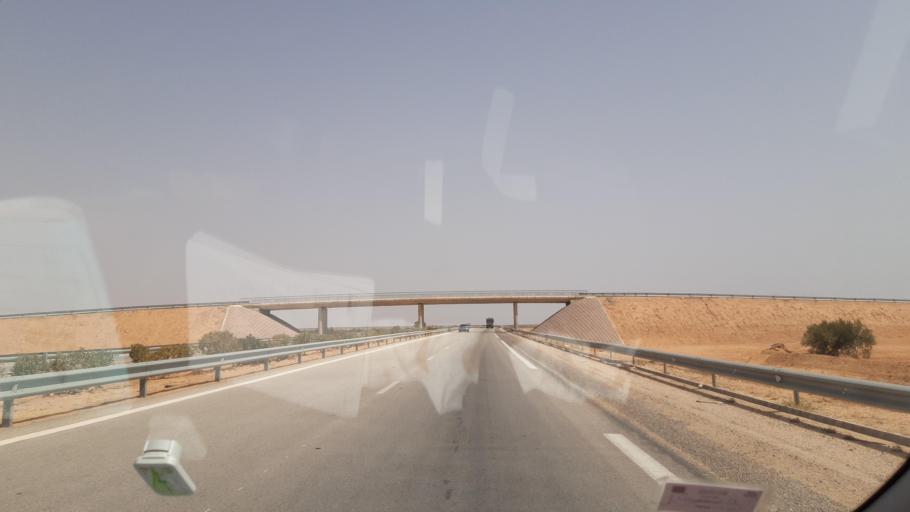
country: TN
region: Safaqis
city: Bi'r `Ali Bin Khalifah
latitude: 34.5285
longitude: 10.1204
